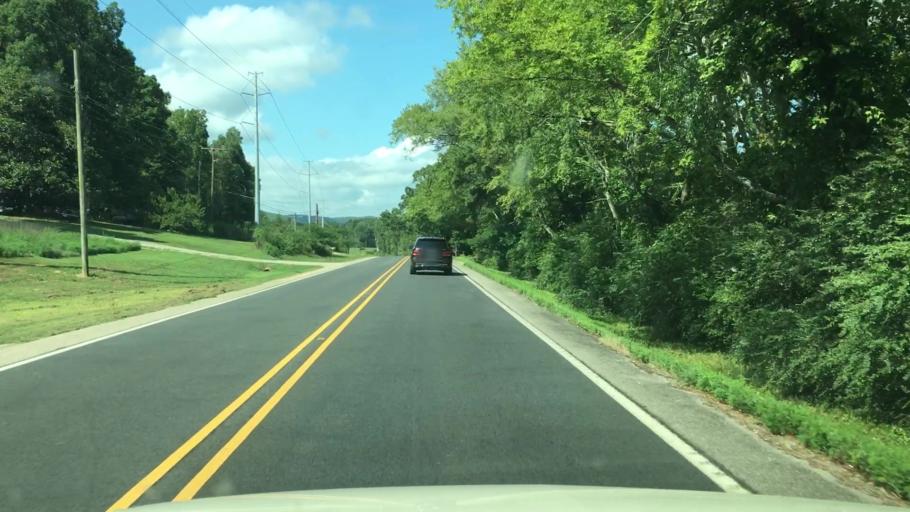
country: US
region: Arkansas
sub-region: Garland County
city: Lake Hamilton
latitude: 34.4015
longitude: -93.0967
